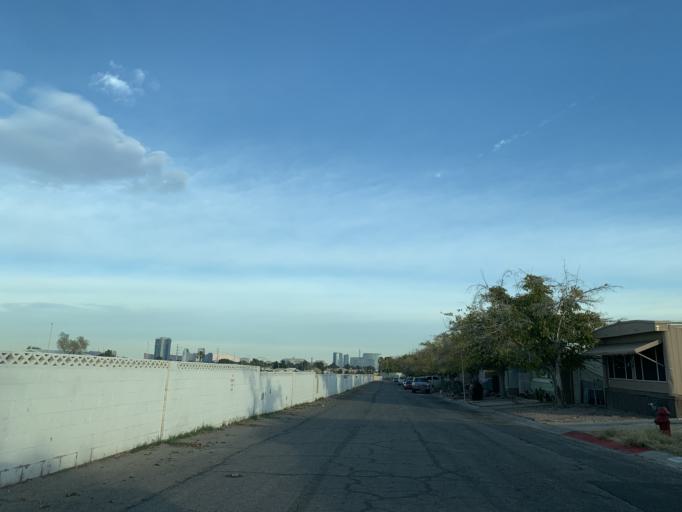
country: US
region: Nevada
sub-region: Clark County
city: Spring Valley
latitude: 36.1036
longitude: -115.2242
